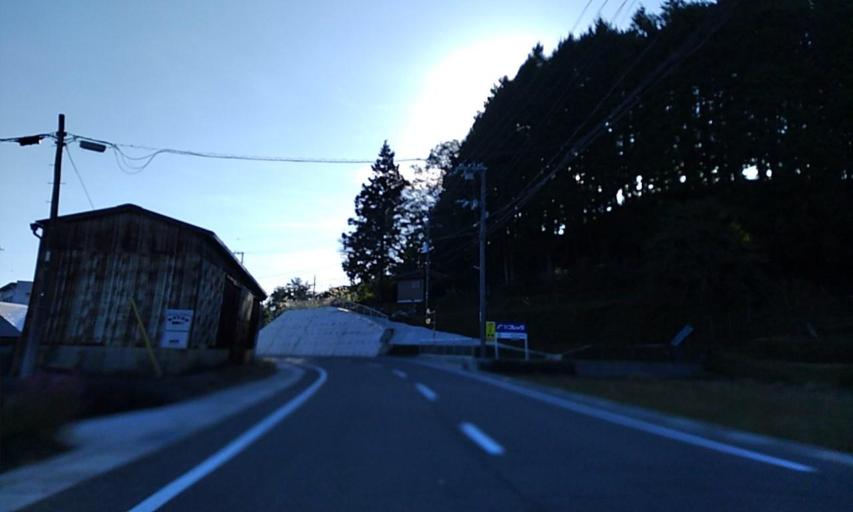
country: JP
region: Wakayama
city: Iwade
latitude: 34.1554
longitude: 135.3035
